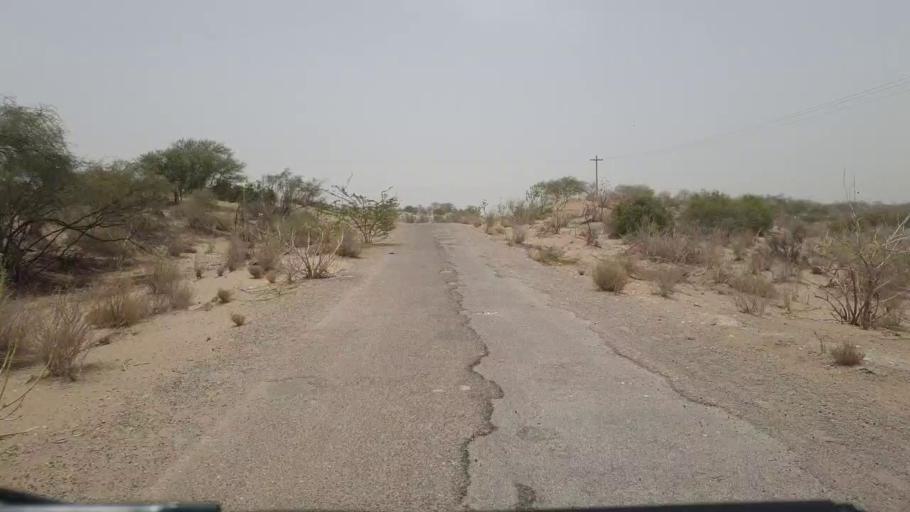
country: PK
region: Sindh
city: Naukot
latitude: 24.7431
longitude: 69.5484
